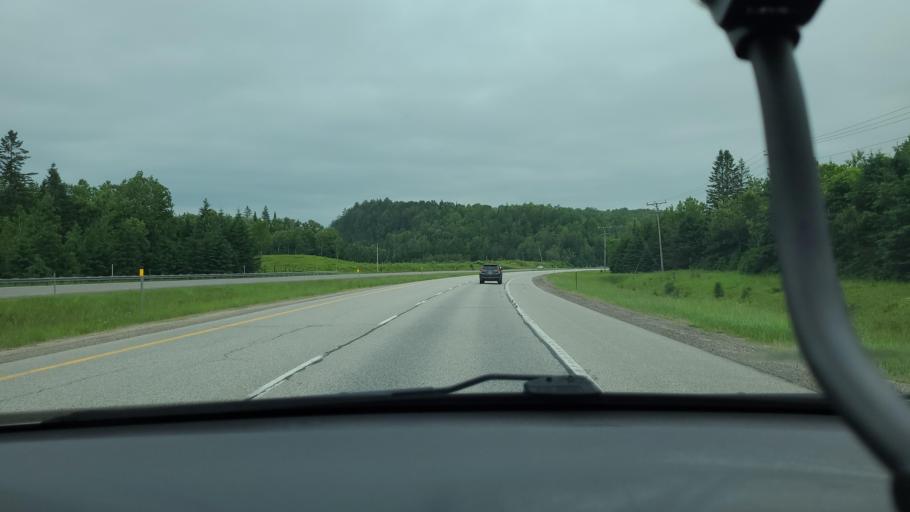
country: CA
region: Quebec
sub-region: Laurentides
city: Labelle
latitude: 46.2277
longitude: -74.7144
